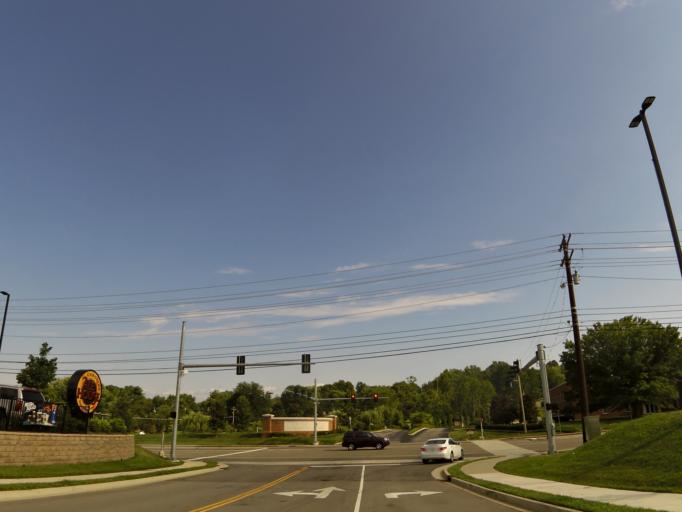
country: US
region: Tennessee
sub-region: Knox County
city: Farragut
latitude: 35.9127
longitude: -84.0843
